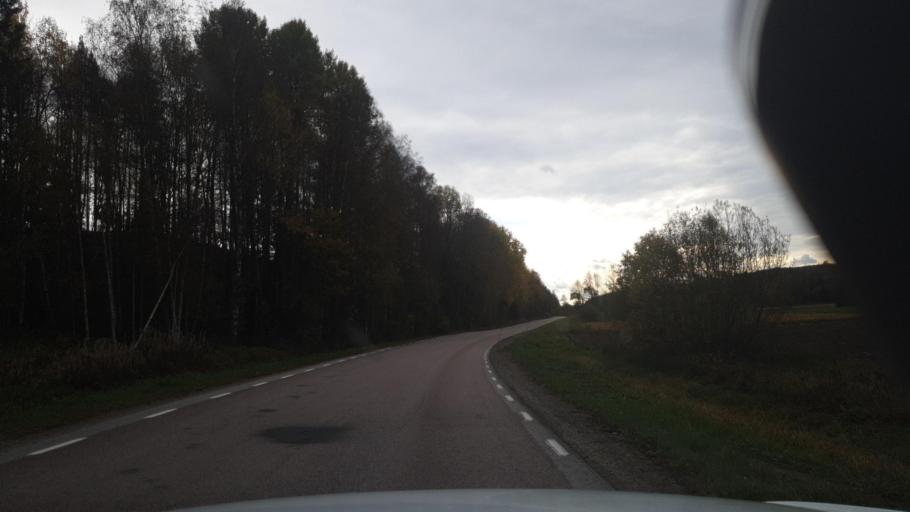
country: SE
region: Vaermland
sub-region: Arvika Kommun
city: Arvika
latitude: 59.6741
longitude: 12.7967
